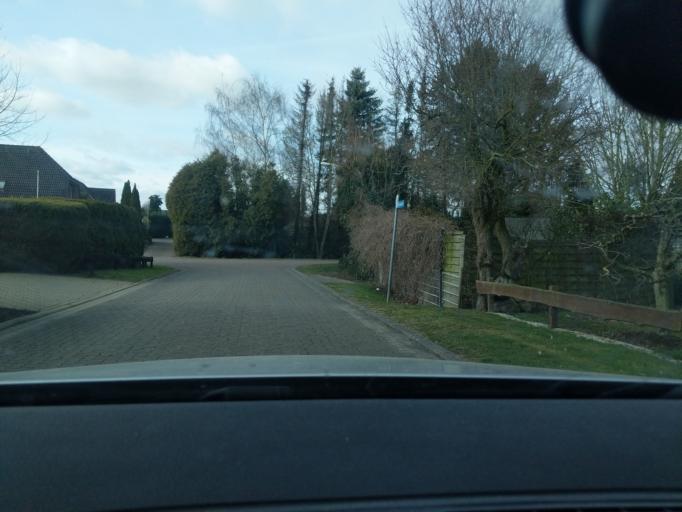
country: DE
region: Lower Saxony
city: Drochtersen
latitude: 53.6904
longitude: 9.4326
